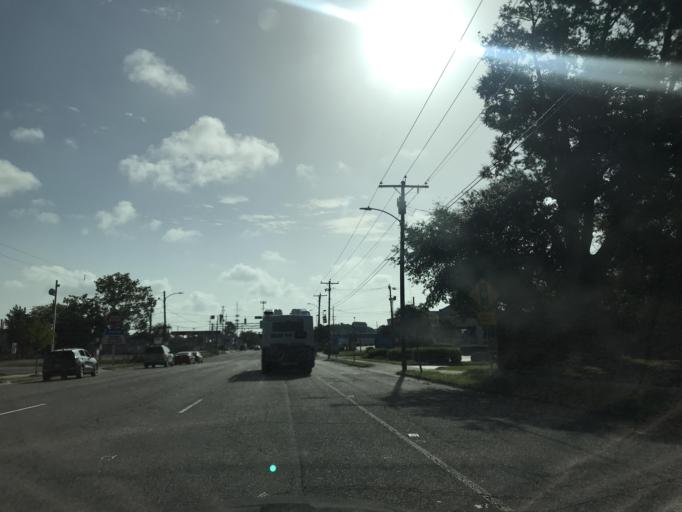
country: US
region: North Carolina
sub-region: New Hanover County
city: Wilmington
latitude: 34.2255
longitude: -77.9285
